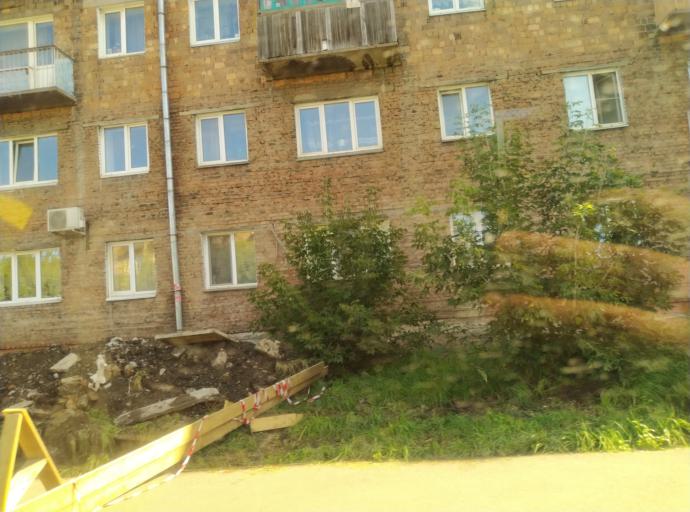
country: RU
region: Krasnoyarskiy
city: Krasnoyarsk
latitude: 55.9784
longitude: 92.8426
